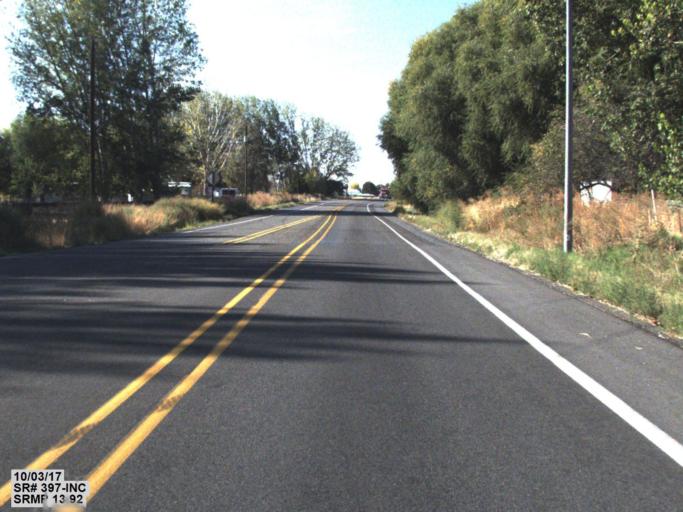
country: US
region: Washington
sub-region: Benton County
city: Finley
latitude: 46.1736
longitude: -119.0553
